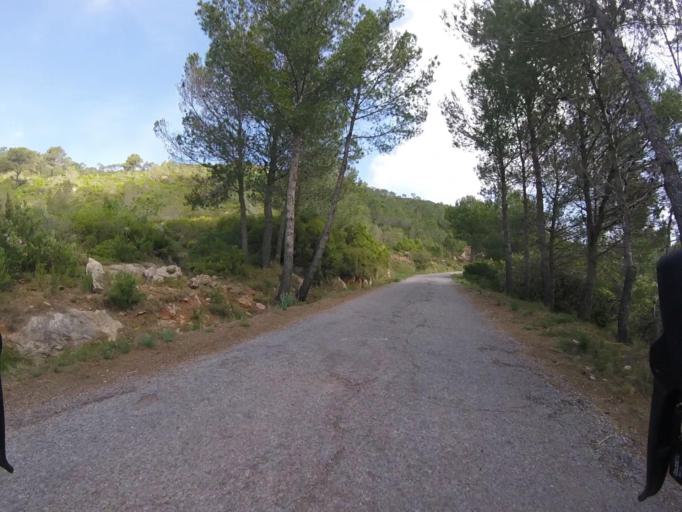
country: ES
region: Valencia
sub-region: Provincia de Castello
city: Benicassim
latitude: 40.0769
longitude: 0.0211
